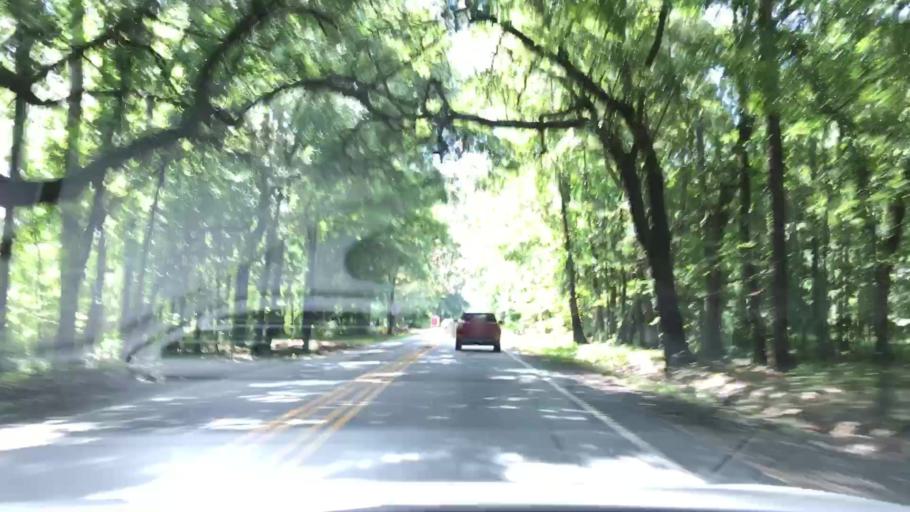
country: US
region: South Carolina
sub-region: Charleston County
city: Shell Point
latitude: 32.8536
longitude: -80.0700
